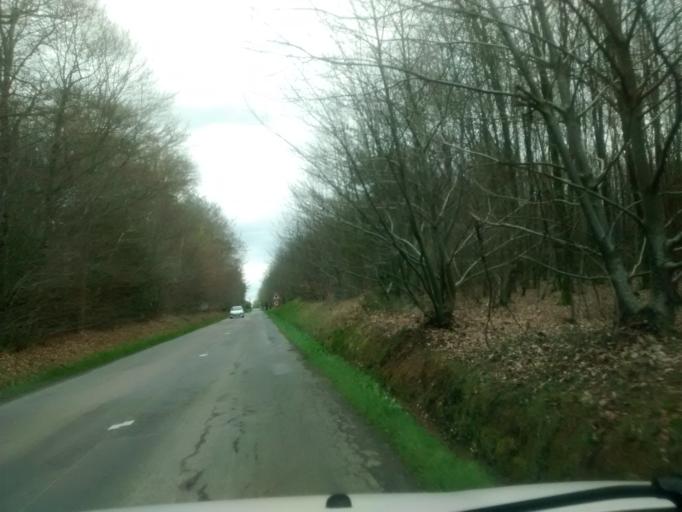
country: FR
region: Brittany
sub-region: Departement d'Ille-et-Vilaine
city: Saint-Sulpice-la-Foret
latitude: 48.1955
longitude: -1.6009
